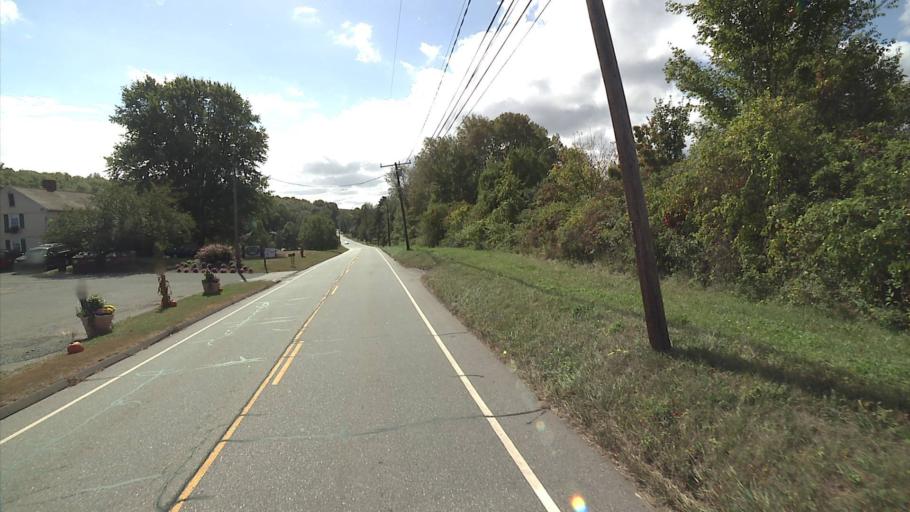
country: US
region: Connecticut
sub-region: Middlesex County
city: Durham
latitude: 41.5242
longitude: -72.7291
